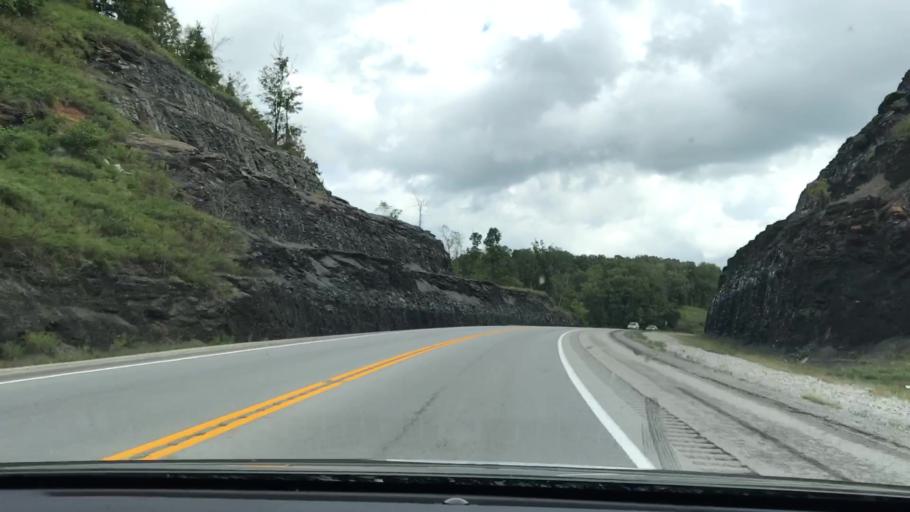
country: US
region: Kentucky
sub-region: Cumberland County
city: Burkesville
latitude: 36.7993
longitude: -85.3838
